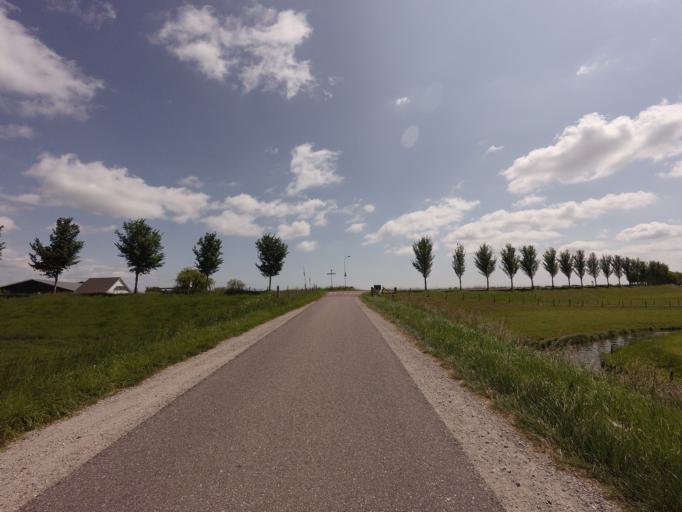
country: NL
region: North Holland
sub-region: Gemeente Beemster
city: Halfweg
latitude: 52.5941
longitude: 4.9484
